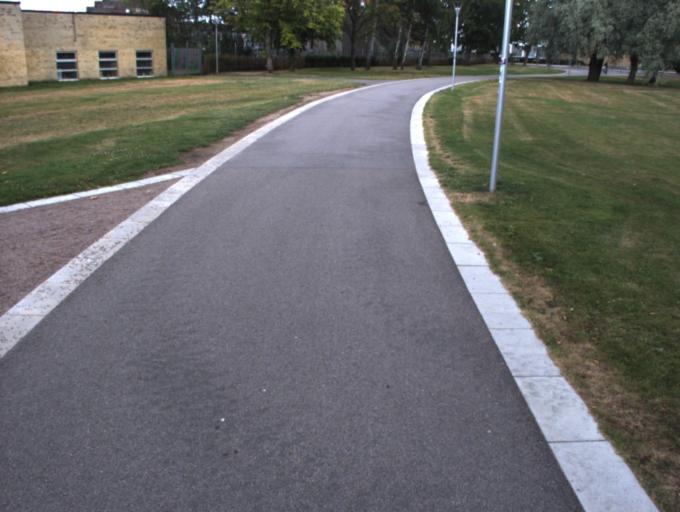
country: SE
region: Skane
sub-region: Helsingborg
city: Helsingborg
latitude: 56.0471
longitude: 12.7103
